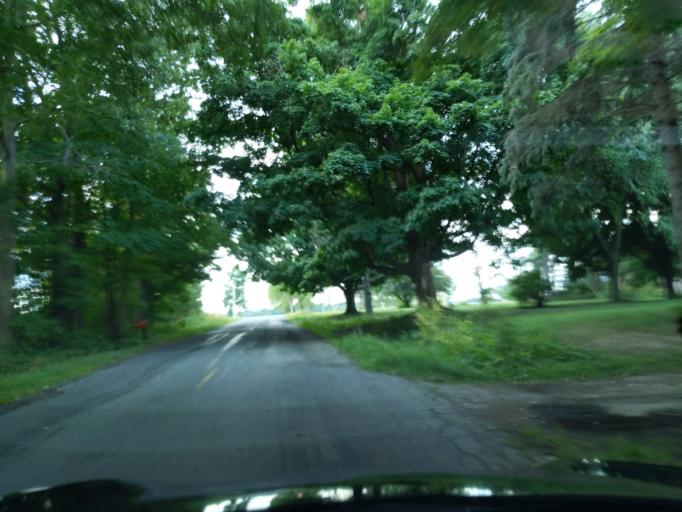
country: US
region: Michigan
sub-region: Eaton County
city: Eaton Rapids
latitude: 42.4449
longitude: -84.5803
